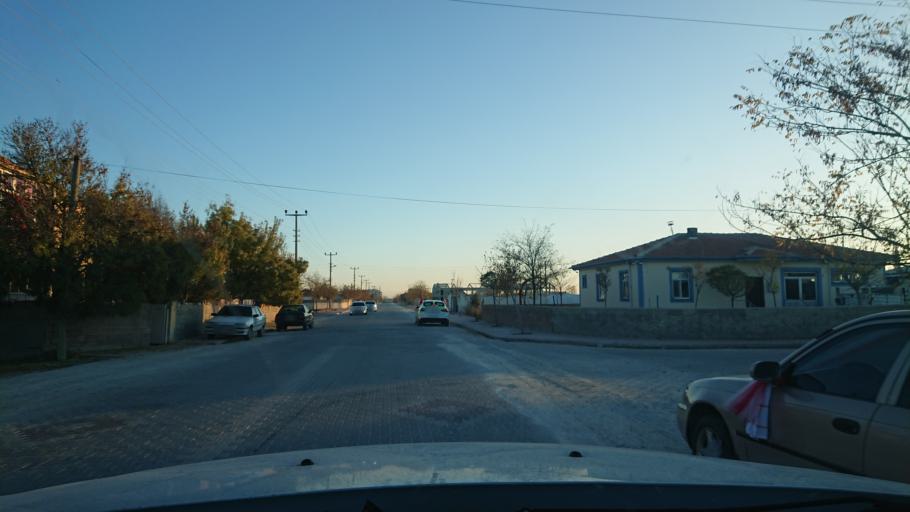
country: TR
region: Aksaray
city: Eskil
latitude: 38.4007
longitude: 33.4201
